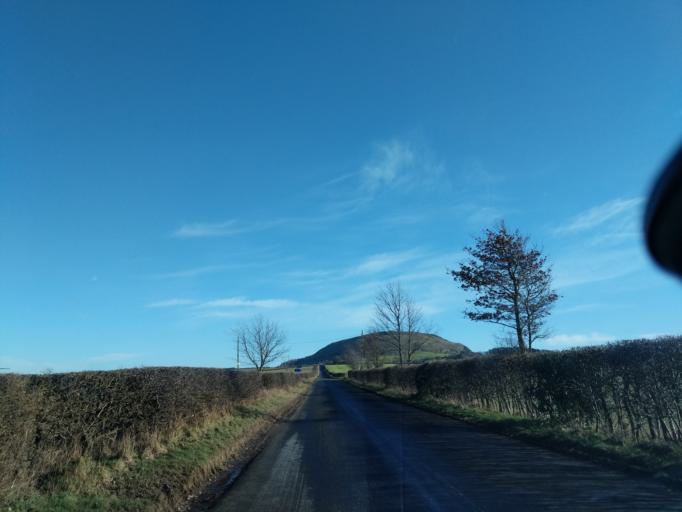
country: GB
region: Scotland
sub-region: East Lothian
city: East Linton
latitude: 55.9643
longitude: -2.7040
